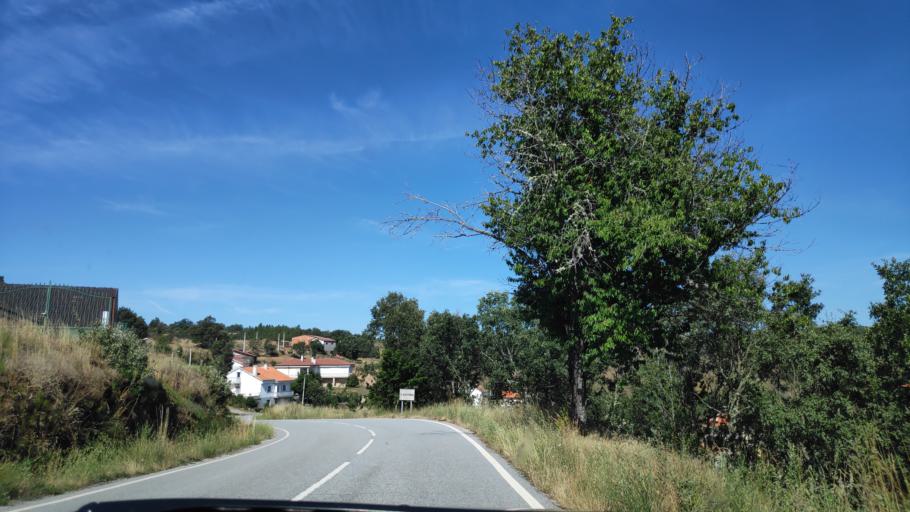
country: ES
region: Castille and Leon
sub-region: Provincia de Zamora
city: Alcanices
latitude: 41.6297
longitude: -6.3507
